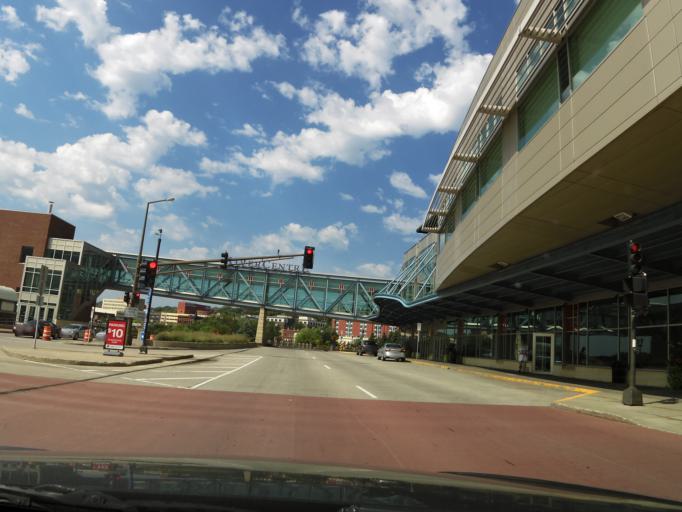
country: US
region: Minnesota
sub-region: Ramsey County
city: Saint Paul
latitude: 44.9436
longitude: -93.0996
